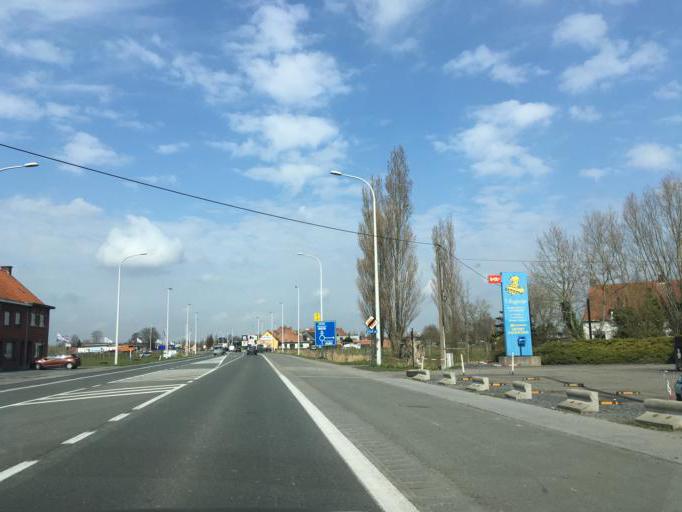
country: BE
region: Flanders
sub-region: Provincie West-Vlaanderen
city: Izegem
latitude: 50.9016
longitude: 3.2243
